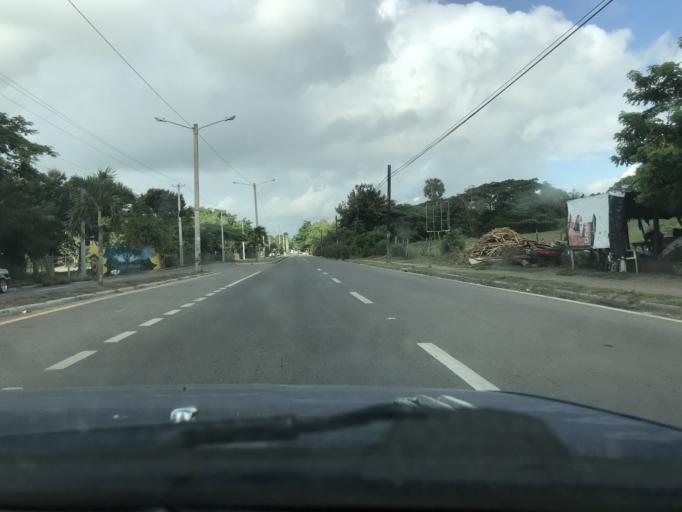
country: DO
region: Santiago
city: Santiago de los Caballeros
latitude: 19.4231
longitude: -70.7334
